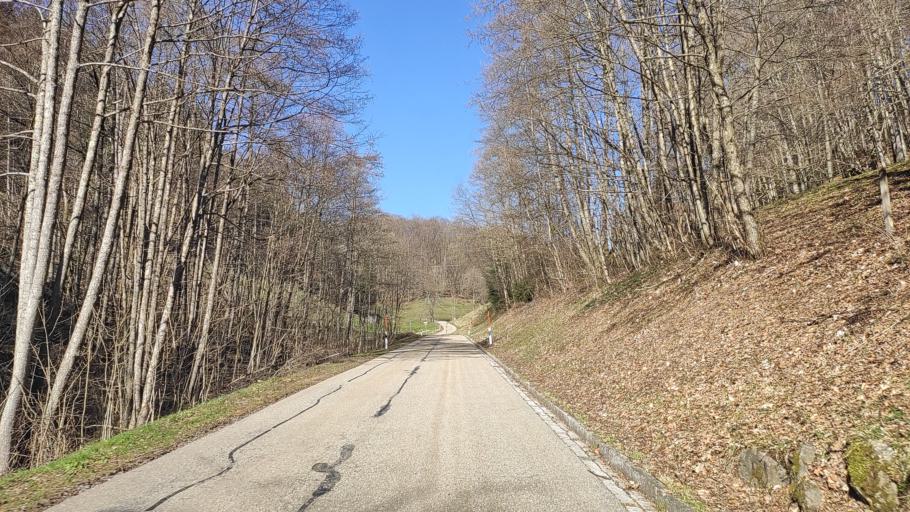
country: DE
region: Baden-Wuerttemberg
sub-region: Freiburg Region
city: Gutach im Breisgau
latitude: 48.1746
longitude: 7.9976
